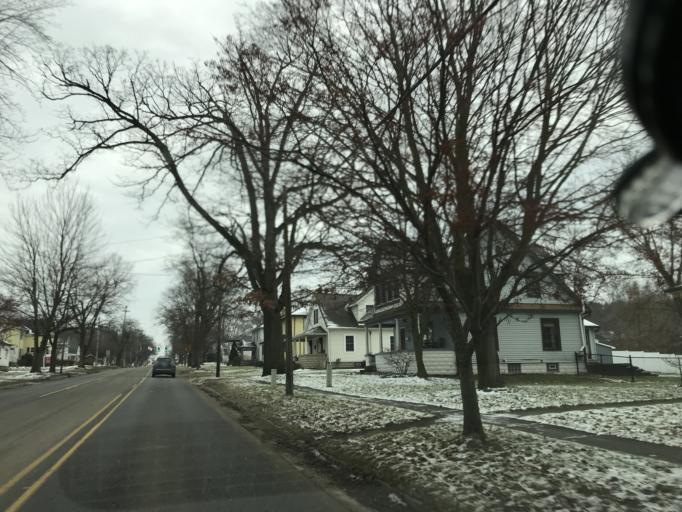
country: US
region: Michigan
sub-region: Kent County
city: Rockford
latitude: 43.1174
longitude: -85.5580
